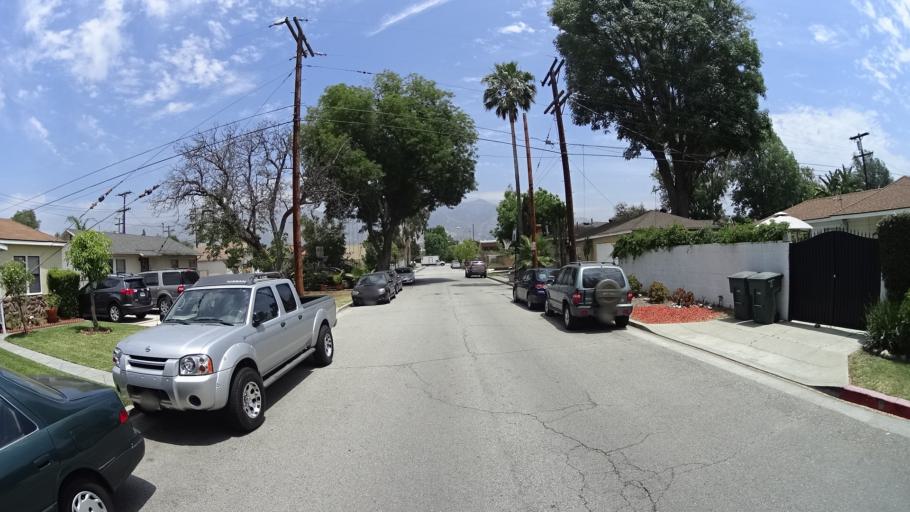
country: US
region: California
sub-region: Los Angeles County
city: North Glendale
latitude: 34.1606
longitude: -118.2908
